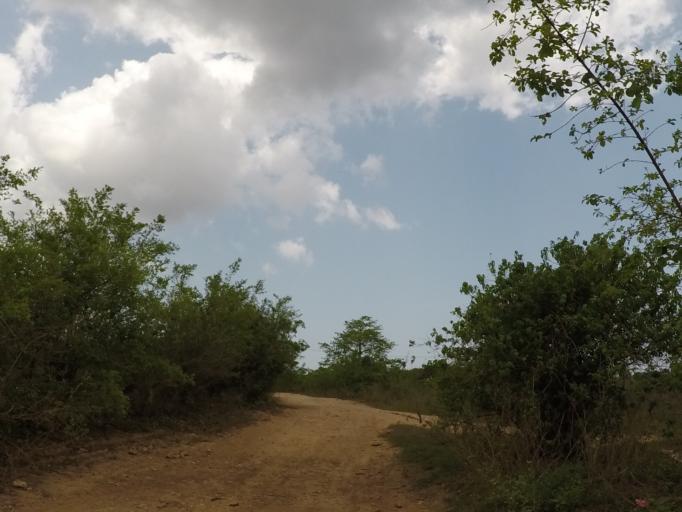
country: TZ
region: Zanzibar Central/South
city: Koani
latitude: -6.1752
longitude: 39.3114
